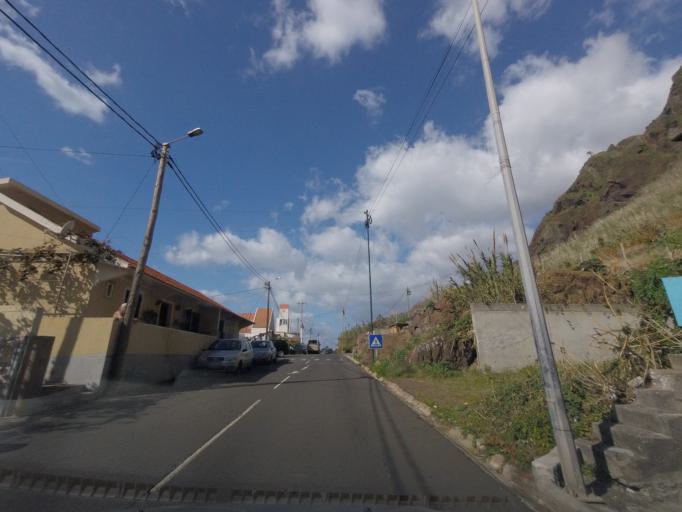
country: PT
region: Madeira
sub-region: Calheta
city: Faja da Ovelha
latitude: 32.7537
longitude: -17.2253
